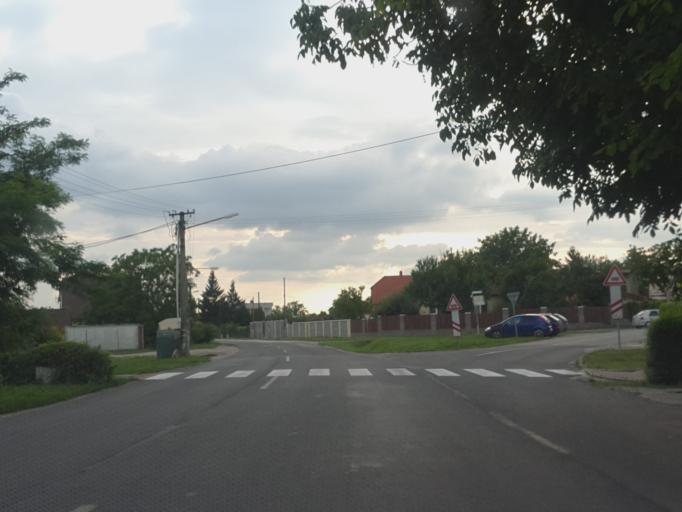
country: SK
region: Bratislavsky
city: Senec
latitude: 48.1967
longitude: 17.3058
